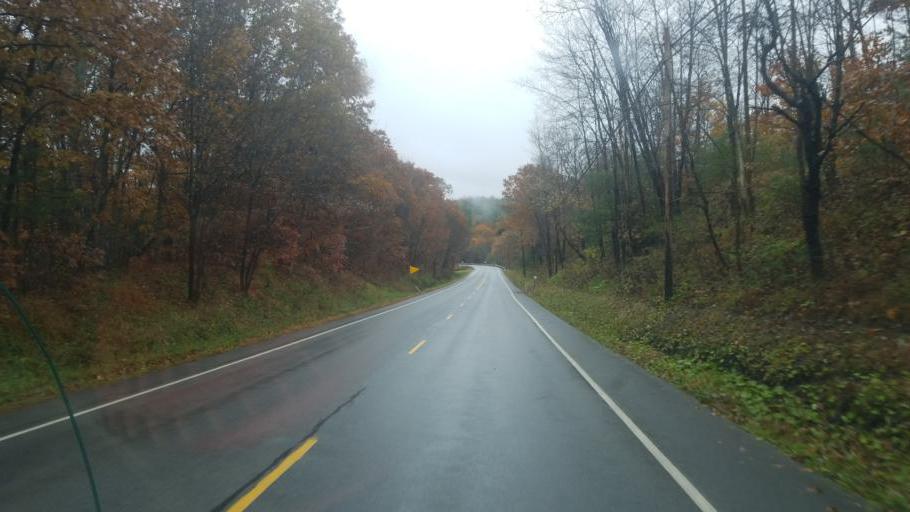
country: US
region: Pennsylvania
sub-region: Clearfield County
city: Shiloh
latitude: 41.1073
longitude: -78.1608
